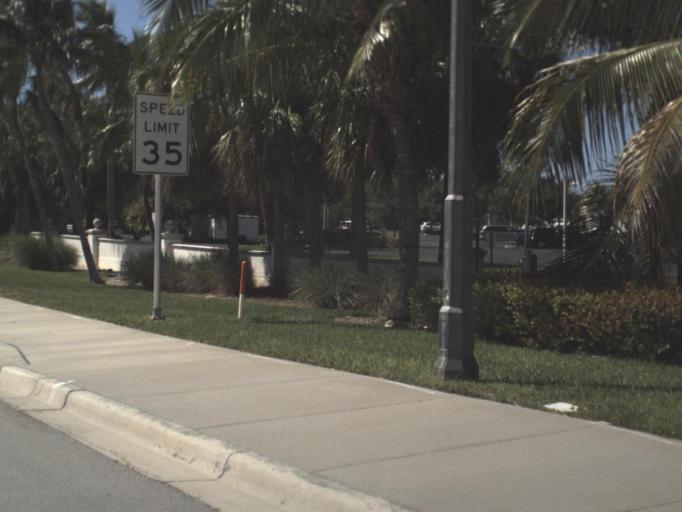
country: US
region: Florida
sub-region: Collier County
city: Marco
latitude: 25.9607
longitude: -81.7111
